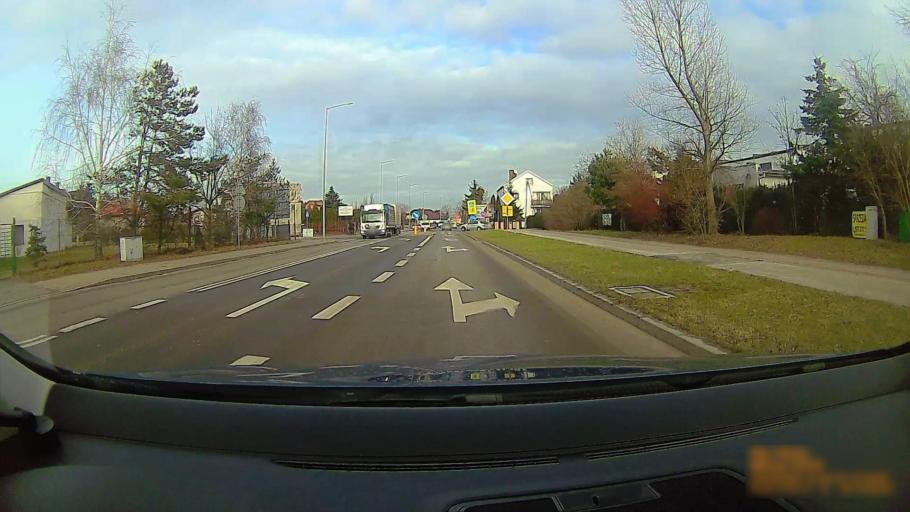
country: PL
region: Greater Poland Voivodeship
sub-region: Konin
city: Konin
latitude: 52.1995
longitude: 18.2427
